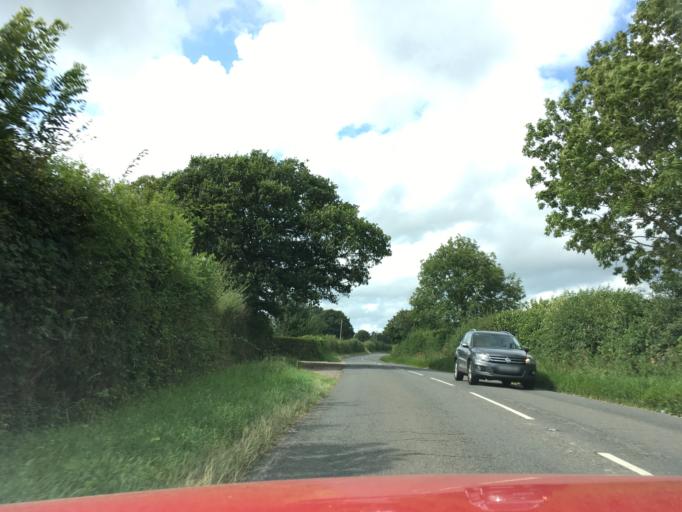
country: GB
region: England
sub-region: Kent
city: Tenterden
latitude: 51.0524
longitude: 0.7325
